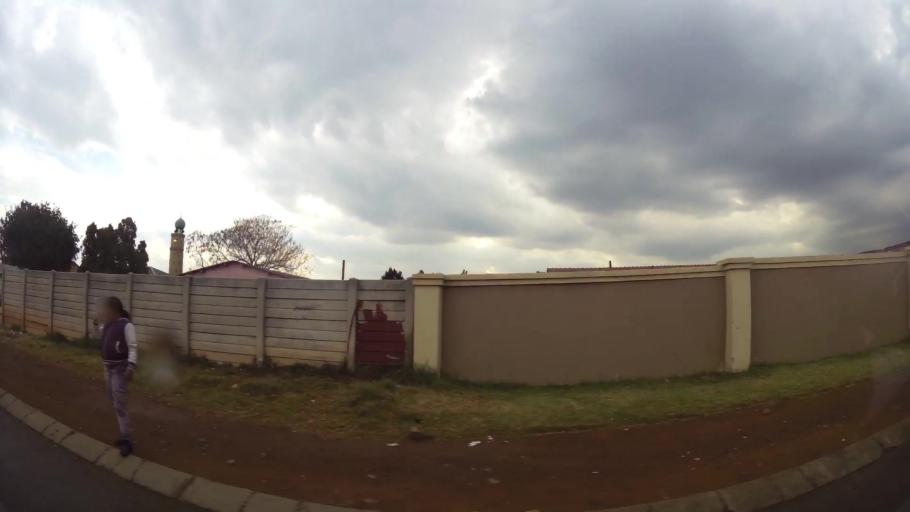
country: ZA
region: Gauteng
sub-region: Ekurhuleni Metropolitan Municipality
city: Germiston
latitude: -26.3726
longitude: 28.1235
